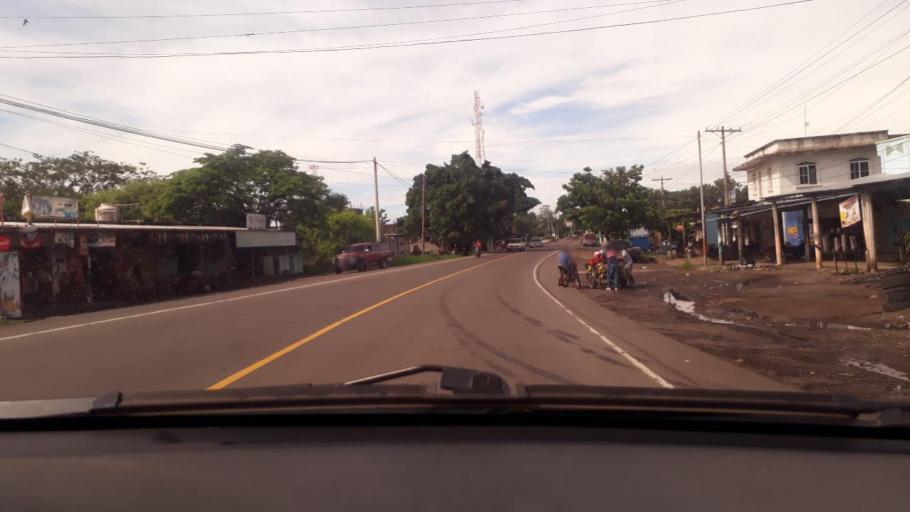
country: SV
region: Ahuachapan
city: San Francisco Menendez
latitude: 13.8787
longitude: -90.0971
